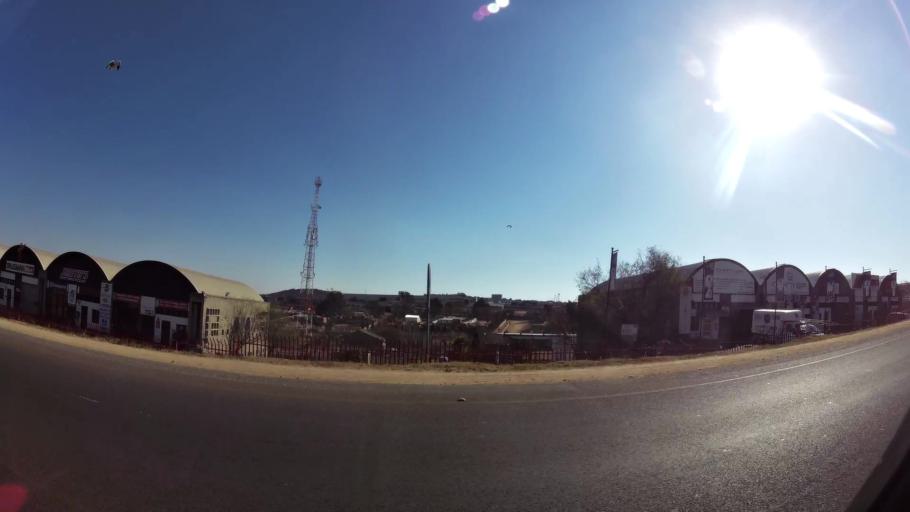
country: ZA
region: Gauteng
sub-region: City of Johannesburg Metropolitan Municipality
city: Midrand
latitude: -25.9991
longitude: 28.0756
